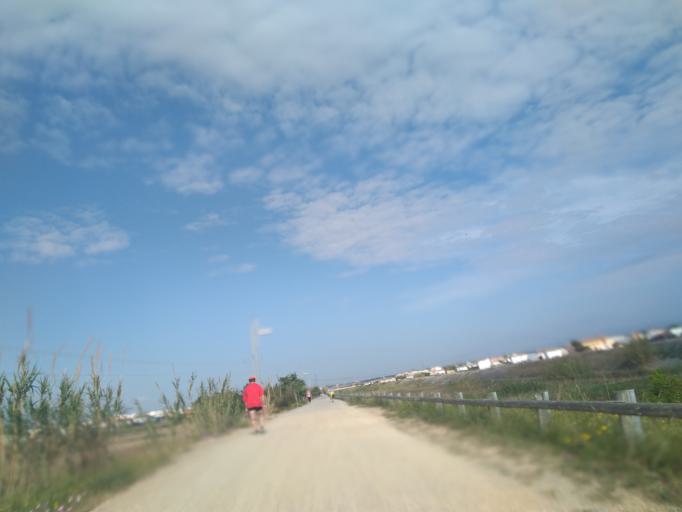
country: ES
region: Valencia
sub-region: Provincia de Valencia
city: Alboraya
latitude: 39.5021
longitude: -0.3317
